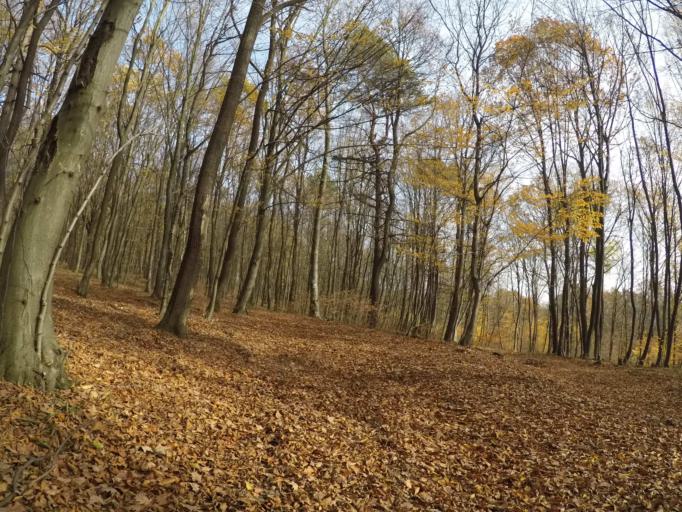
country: SK
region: Presovsky
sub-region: Okres Presov
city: Presov
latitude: 48.9276
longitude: 21.2193
